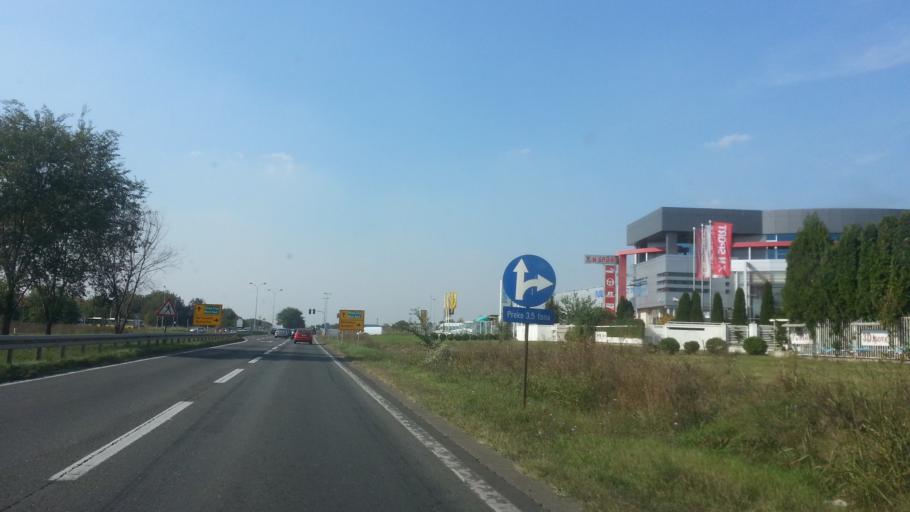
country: RS
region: Central Serbia
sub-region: Belgrade
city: Zemun
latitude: 44.8709
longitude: 20.3362
